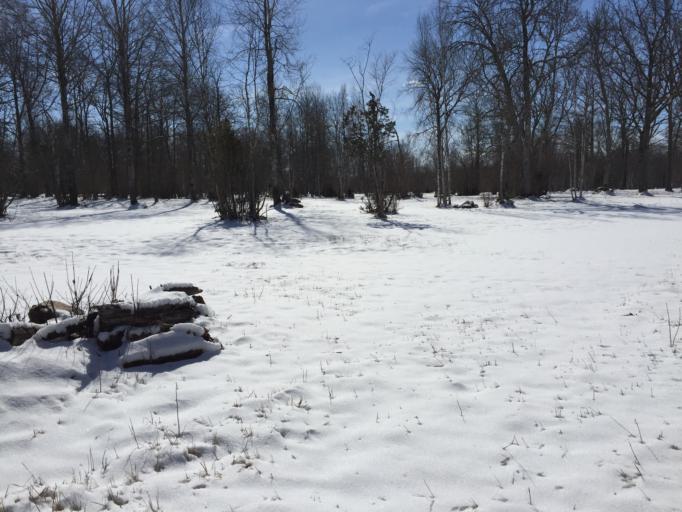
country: EE
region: Laeaene
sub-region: Lihula vald
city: Lihula
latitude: 58.5371
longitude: 24.0740
